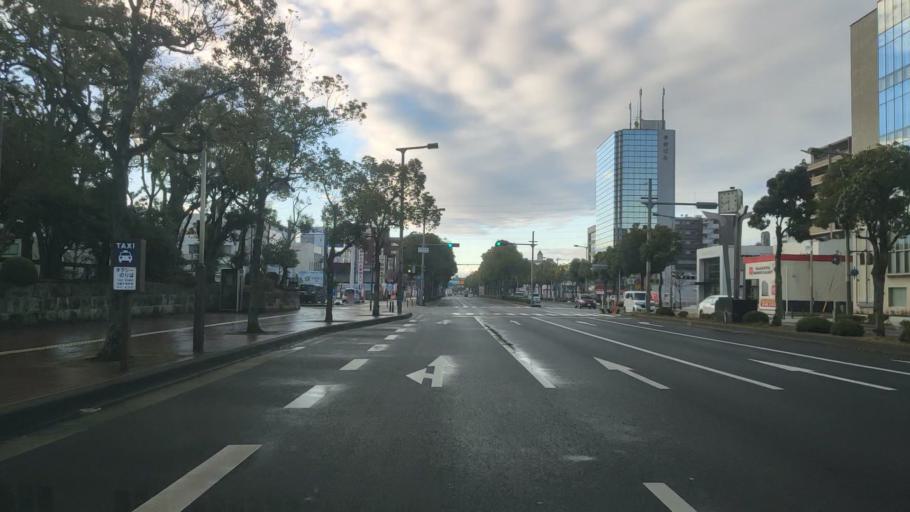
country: JP
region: Hyogo
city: Himeji
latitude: 34.8157
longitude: 134.6845
